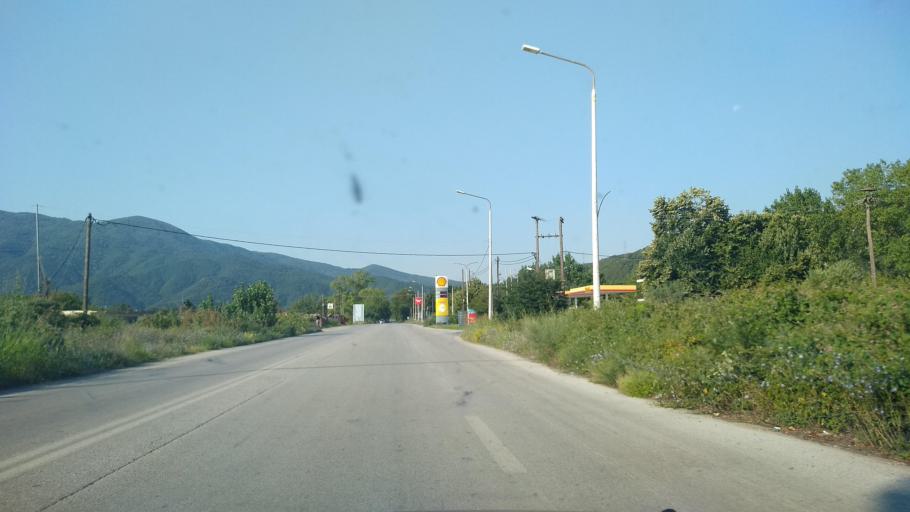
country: GR
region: Central Macedonia
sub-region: Nomos Thessalonikis
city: Nea Vrasna
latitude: 40.6888
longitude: 23.6818
